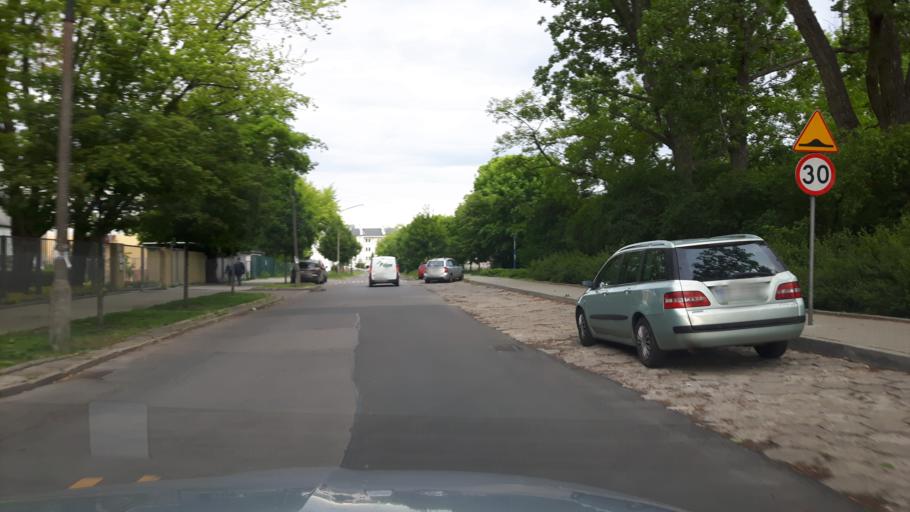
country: PL
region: Masovian Voivodeship
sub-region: Warszawa
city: Praga Poludnie
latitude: 52.2435
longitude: 21.1120
